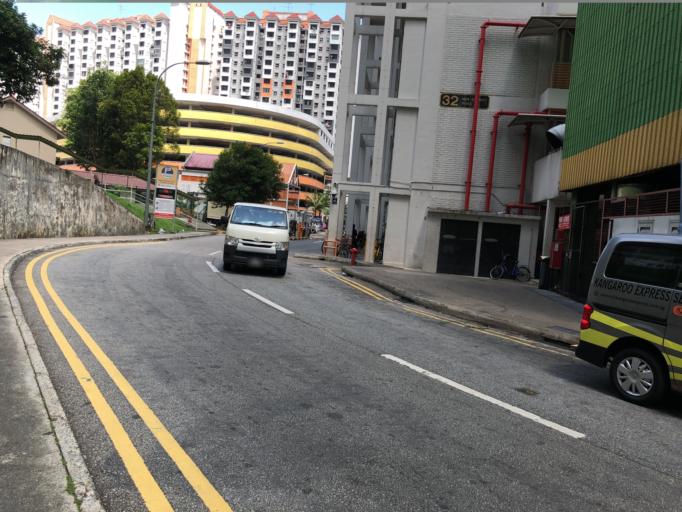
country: SG
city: Singapore
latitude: 1.2844
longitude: 103.8420
